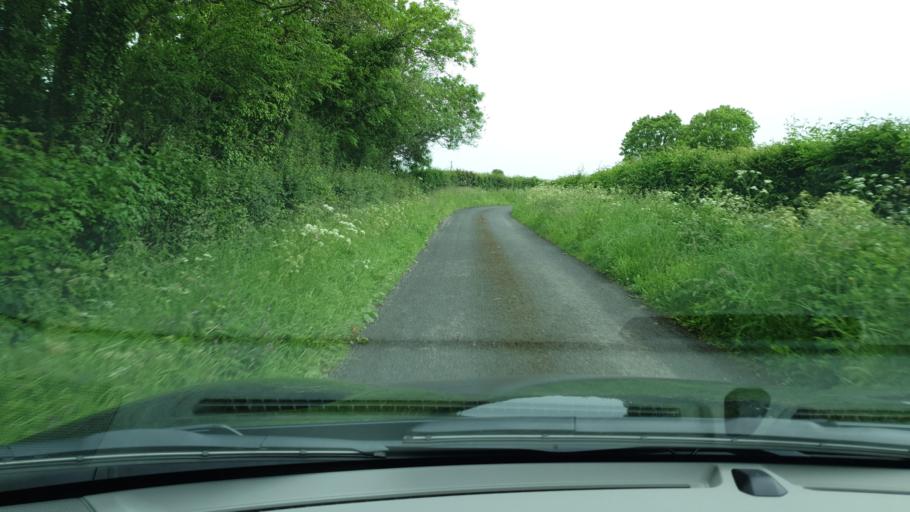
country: IE
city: Confey
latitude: 53.4238
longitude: -6.5311
